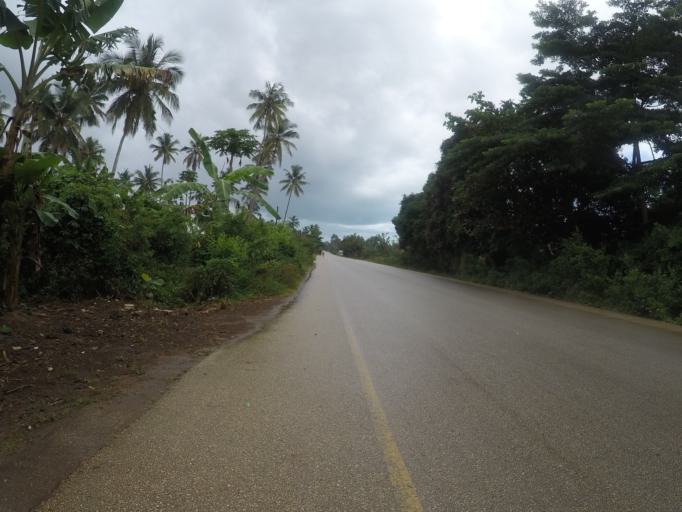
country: TZ
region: Zanzibar North
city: Mkokotoni
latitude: -5.9782
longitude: 39.1961
